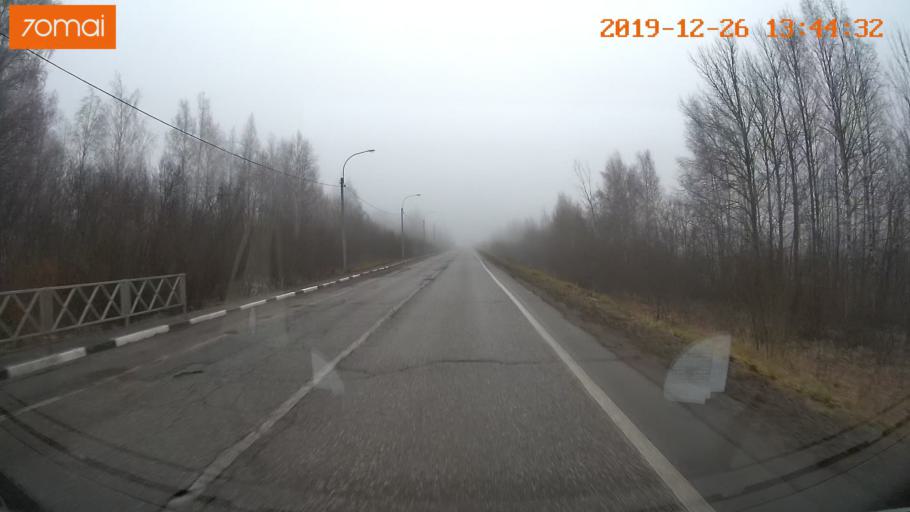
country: RU
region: Vologda
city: Sheksna
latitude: 58.7012
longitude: 38.5077
